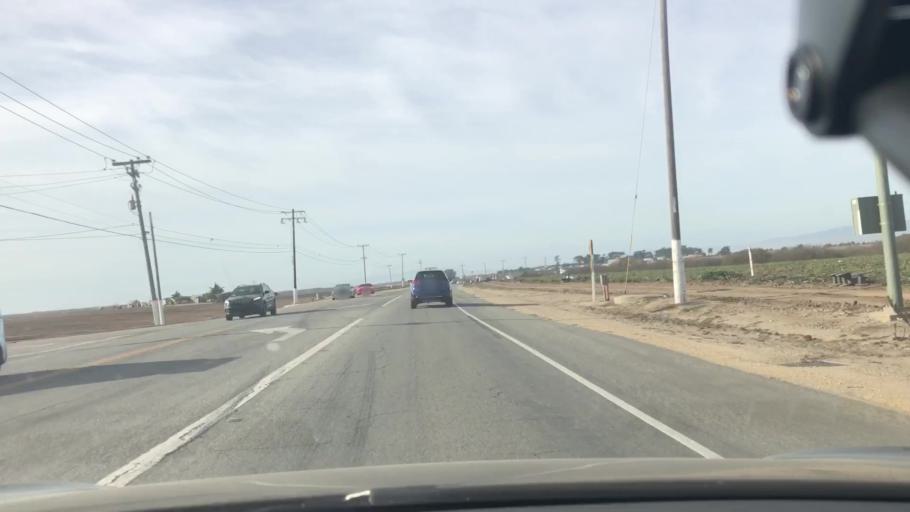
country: US
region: California
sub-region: Monterey County
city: Castroville
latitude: 36.7802
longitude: -121.7775
